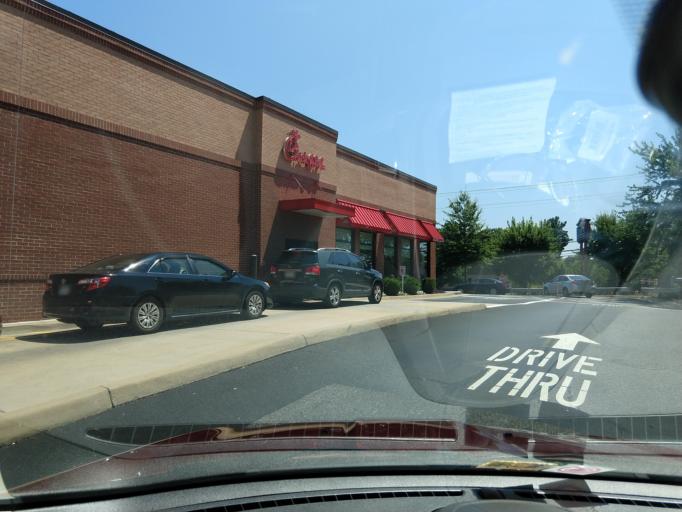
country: US
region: Virginia
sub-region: Albemarle County
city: Hollymead
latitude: 38.0885
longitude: -78.4711
